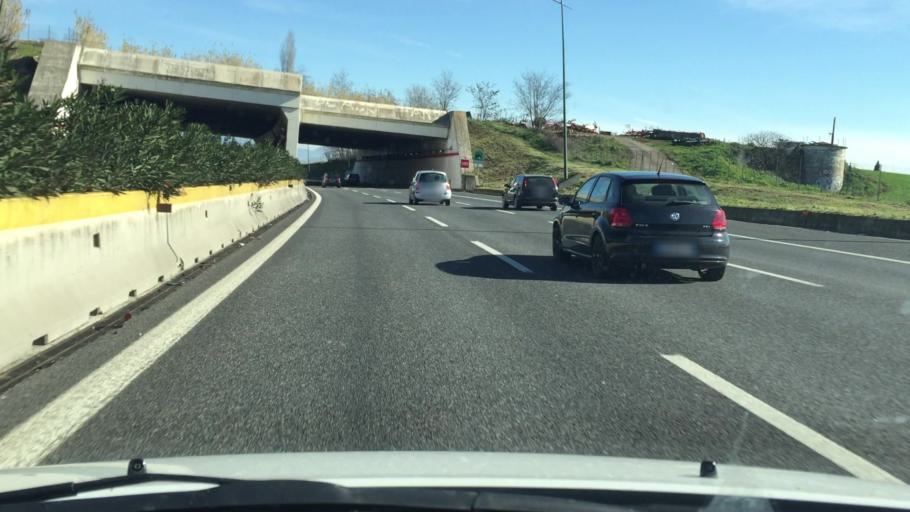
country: VA
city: Vatican City
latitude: 41.9815
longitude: 12.4579
